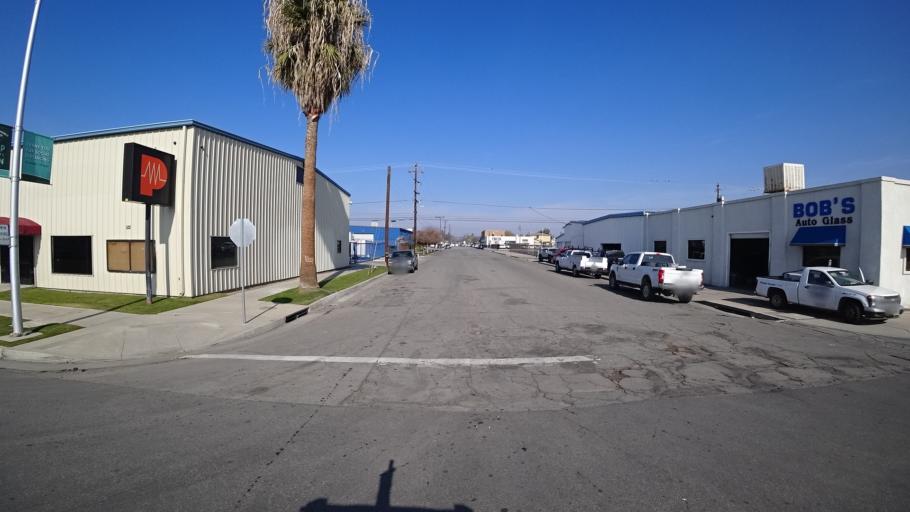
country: US
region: California
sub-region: Kern County
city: Bakersfield
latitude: 35.3752
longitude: -118.9952
